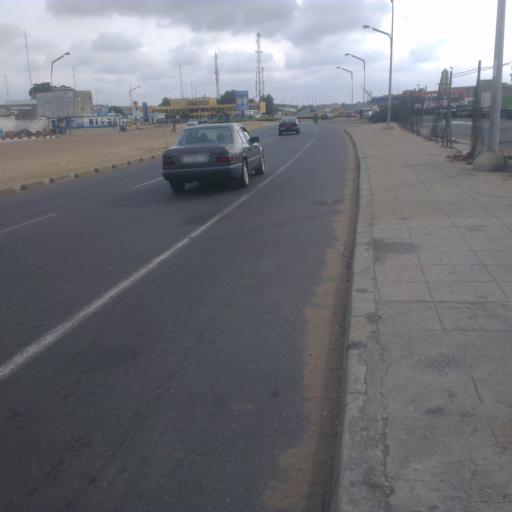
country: TG
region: Maritime
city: Lome
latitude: 6.1411
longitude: 1.2743
